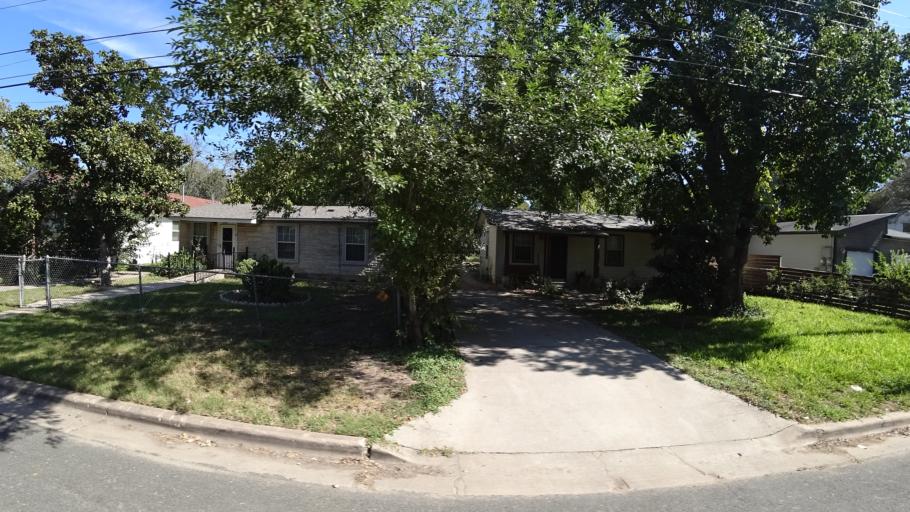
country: US
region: Texas
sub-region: Travis County
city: Austin
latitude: 30.2685
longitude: -97.6845
